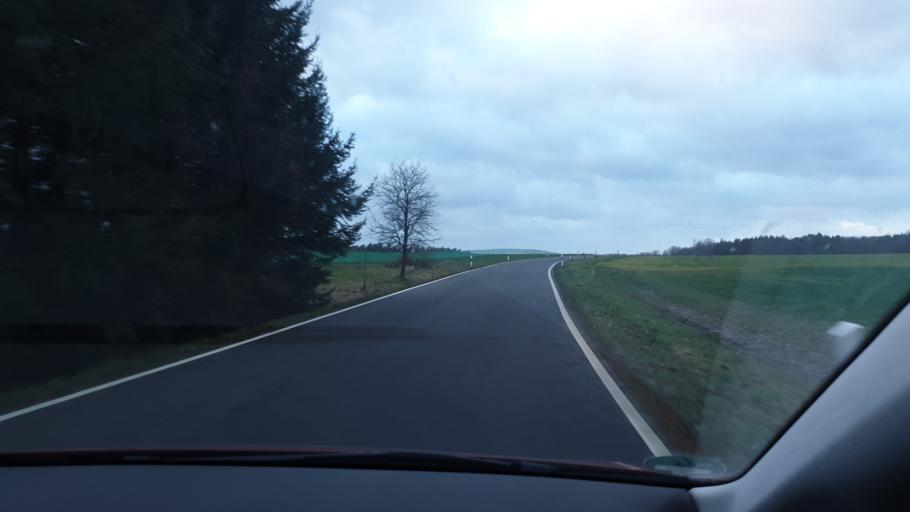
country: DE
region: Saxony
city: Falkenhain
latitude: 51.4522
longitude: 12.8610
